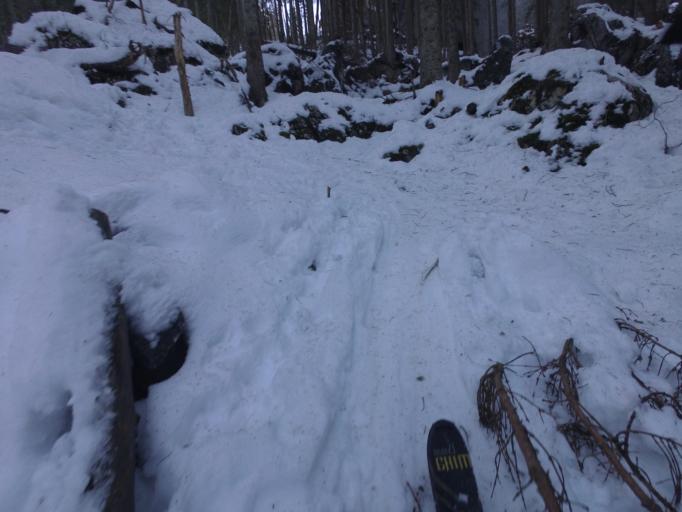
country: AT
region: Salzburg
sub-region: Politischer Bezirk Hallein
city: Scheffau am Tennengebirge
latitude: 47.6363
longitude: 13.2499
